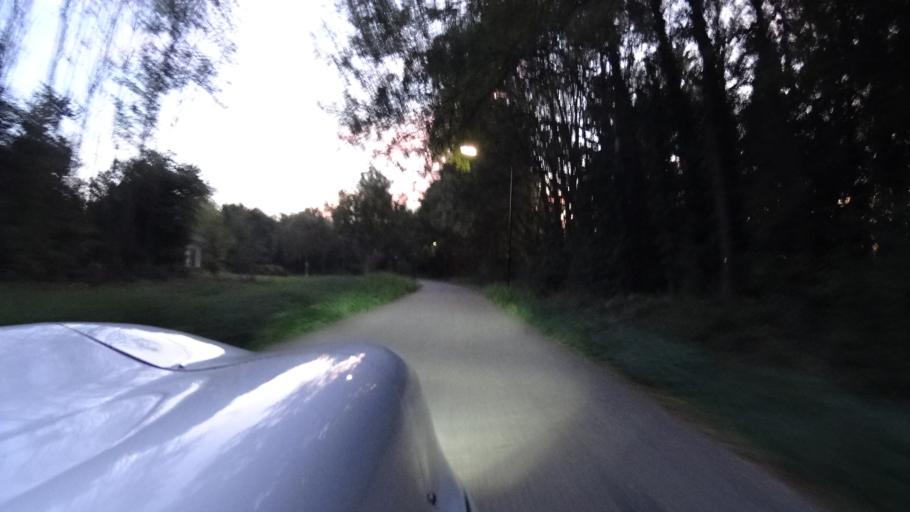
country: NL
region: North Brabant
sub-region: Gemeente Aalburg
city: Aalburg
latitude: 51.7435
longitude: 5.1011
